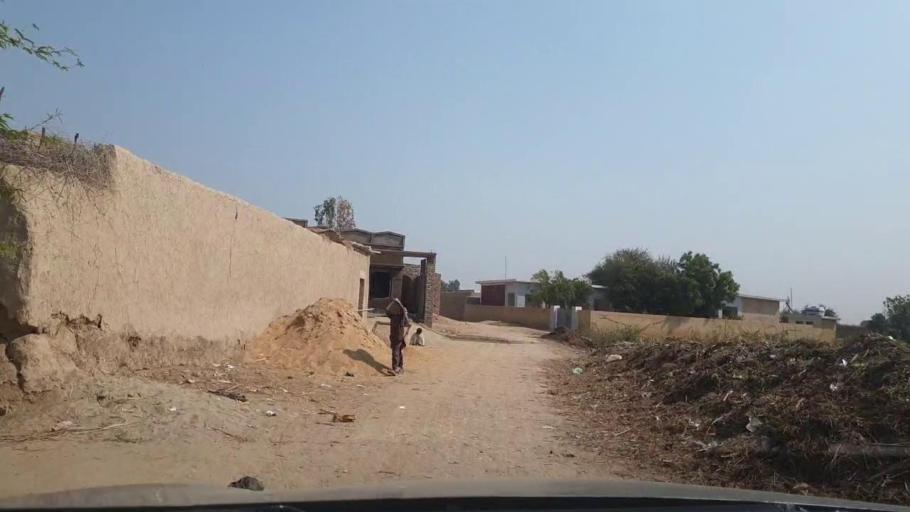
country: PK
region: Sindh
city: Tando Allahyar
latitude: 25.5518
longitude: 68.8197
